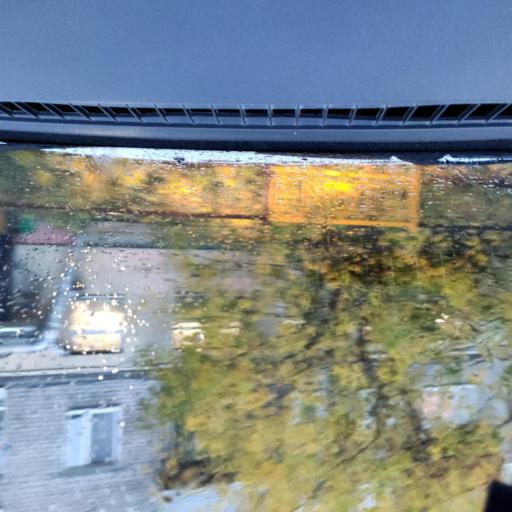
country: RU
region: Perm
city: Kultayevo
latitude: 58.0069
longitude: 55.9555
